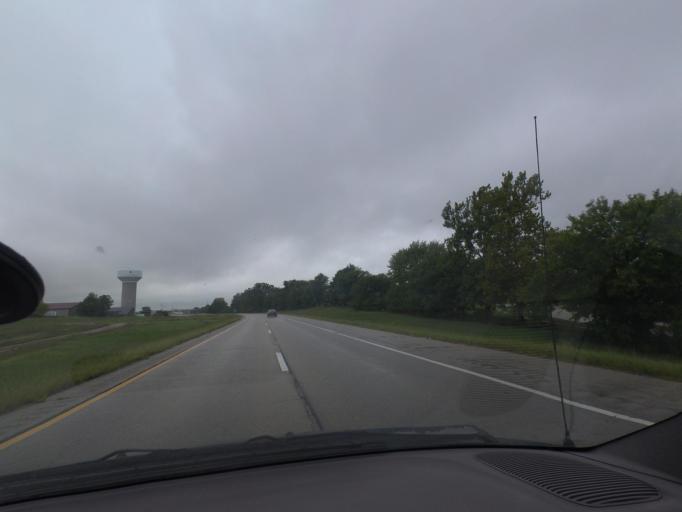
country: US
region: Illinois
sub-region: Champaign County
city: Champaign
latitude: 40.1194
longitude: -88.2887
